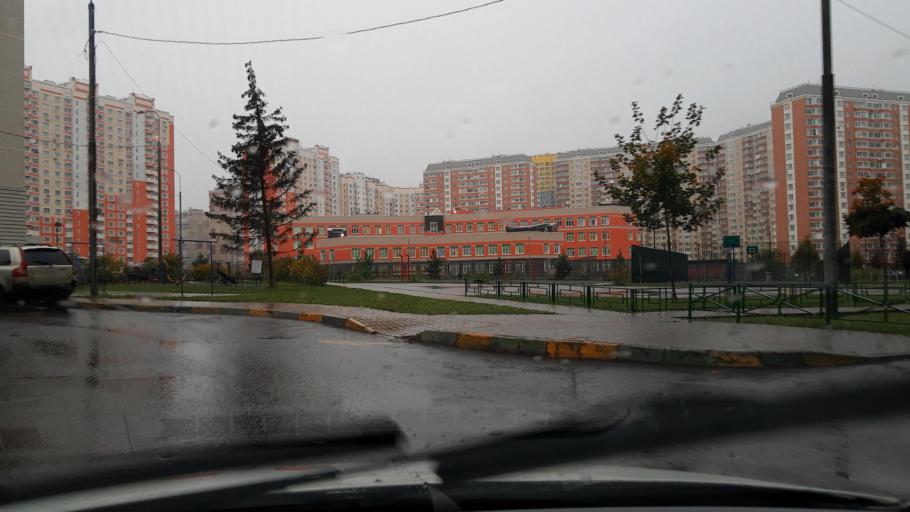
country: RU
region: Moskovskaya
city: Shcherbinka
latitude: 55.5207
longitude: 37.5957
